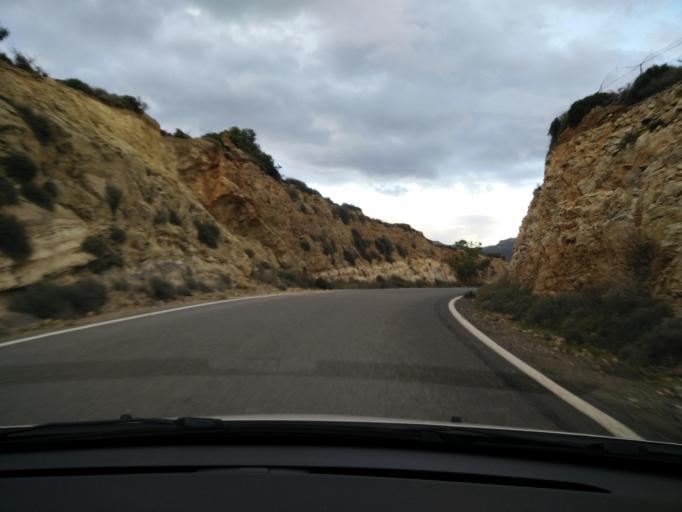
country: GR
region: Crete
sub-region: Nomos Lasithiou
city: Gra Liyia
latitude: 35.0882
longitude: 25.7048
